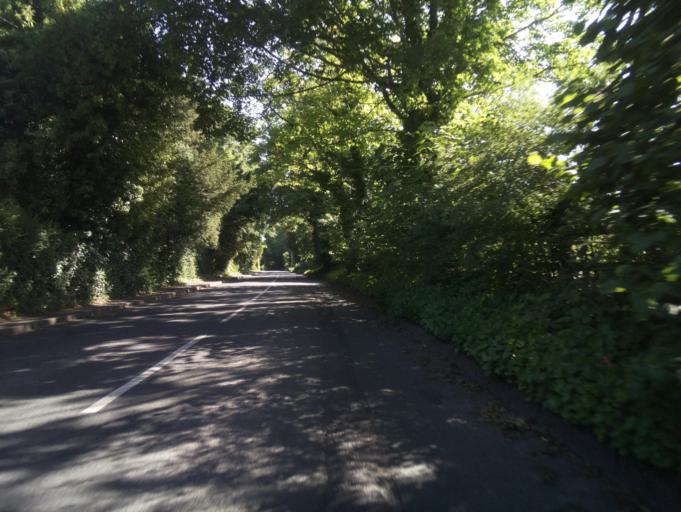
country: GB
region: England
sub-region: Hampshire
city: Winchester
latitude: 51.0814
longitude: -1.3411
